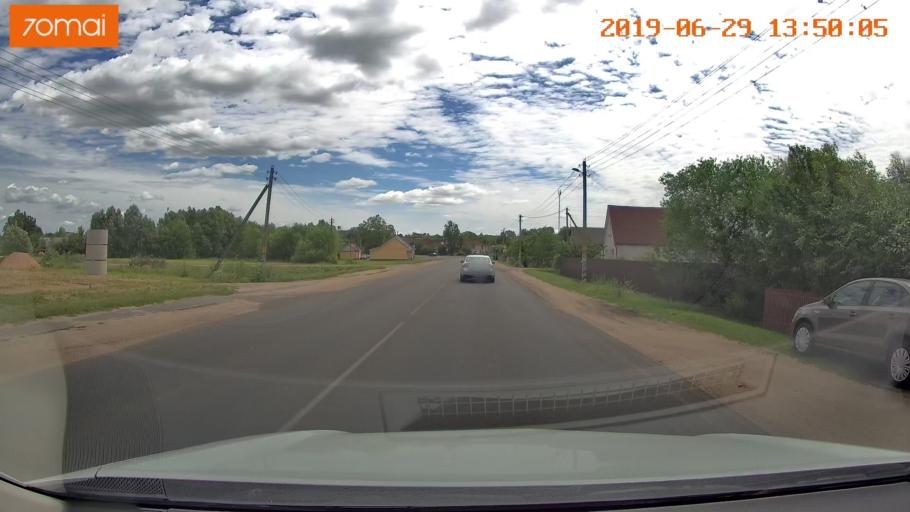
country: BY
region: Minsk
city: Slutsk
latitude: 53.0052
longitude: 27.5666
